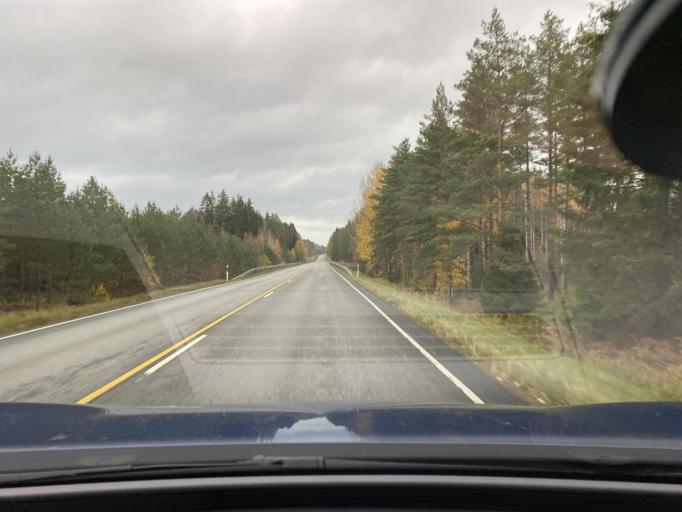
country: FI
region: Varsinais-Suomi
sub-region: Loimaa
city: Ylaene
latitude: 60.8923
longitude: 22.4046
